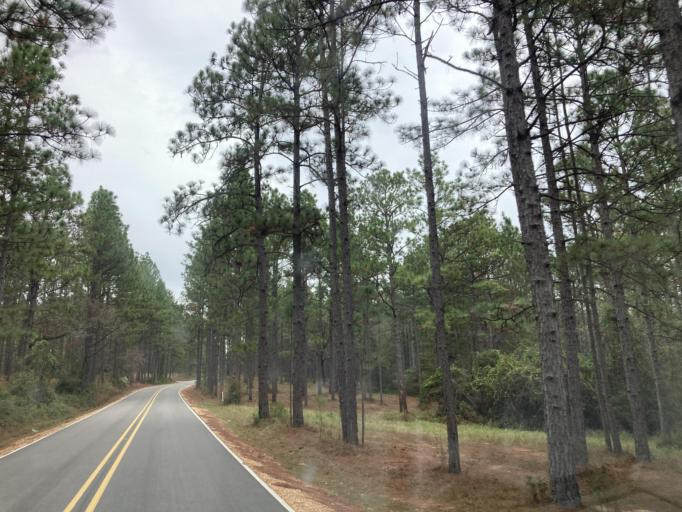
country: US
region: Mississippi
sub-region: Lamar County
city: Purvis
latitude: 31.1082
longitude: -89.4300
